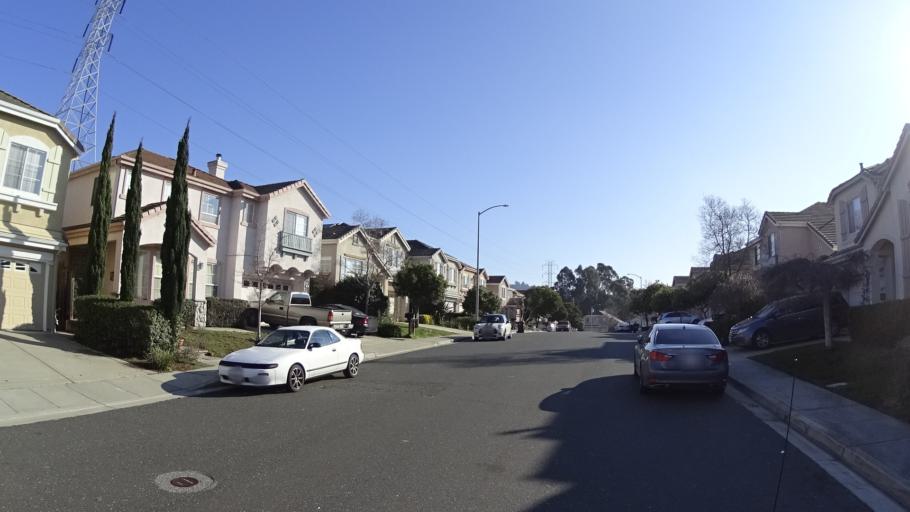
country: US
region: California
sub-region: Alameda County
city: Fairview
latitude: 37.6915
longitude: -122.0431
